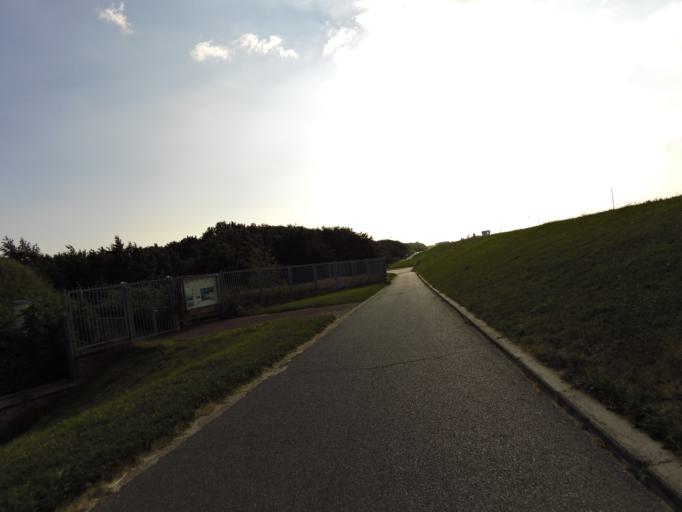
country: DE
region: Lower Saxony
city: Cuxhaven
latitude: 53.8916
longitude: 8.6803
